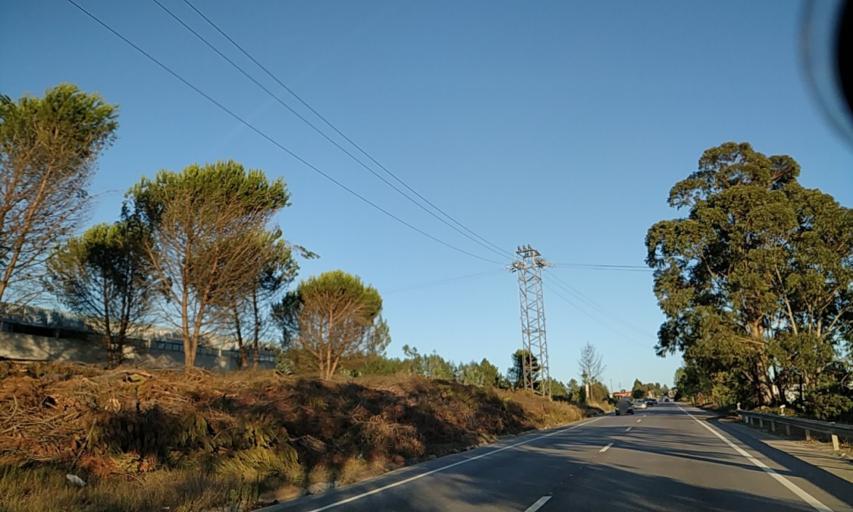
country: PT
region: Aveiro
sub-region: Oliveira do Bairro
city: Oia
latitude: 40.5545
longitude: -8.5504
